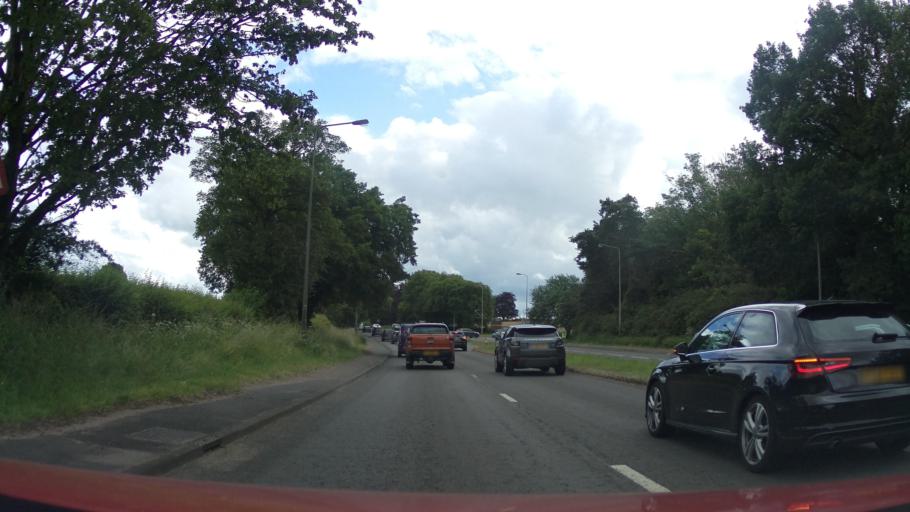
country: GB
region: England
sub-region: Dudley
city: Kingswinford
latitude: 52.4583
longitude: -2.2055
